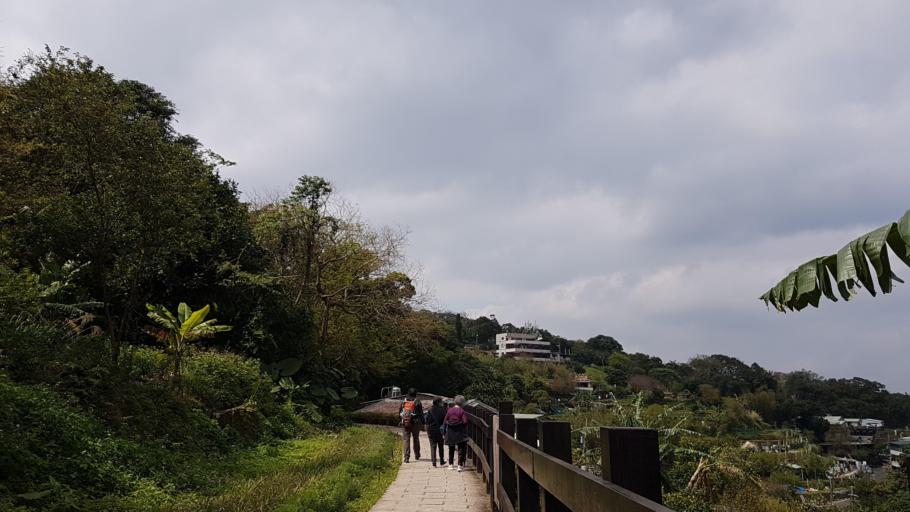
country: TW
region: Taipei
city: Taipei
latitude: 24.9674
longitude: 121.5827
